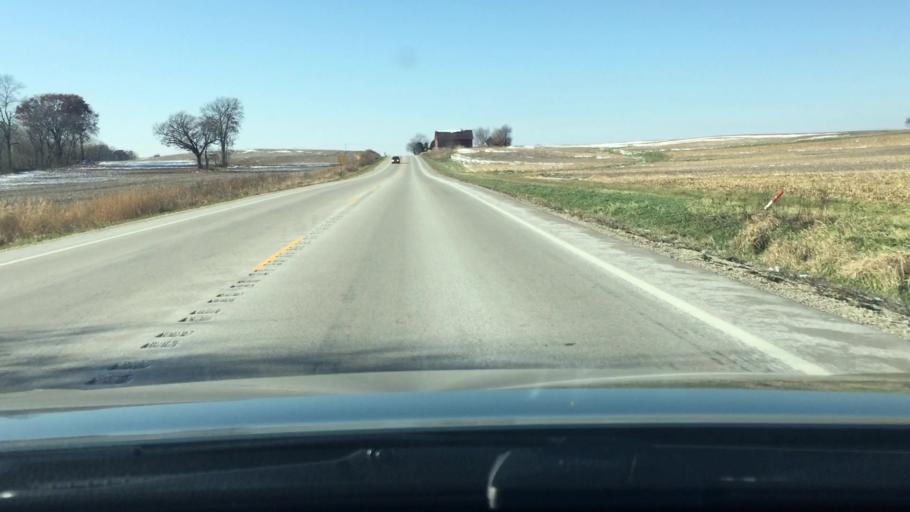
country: US
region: Wisconsin
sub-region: Jefferson County
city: Lake Mills
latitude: 43.0078
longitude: -88.8867
